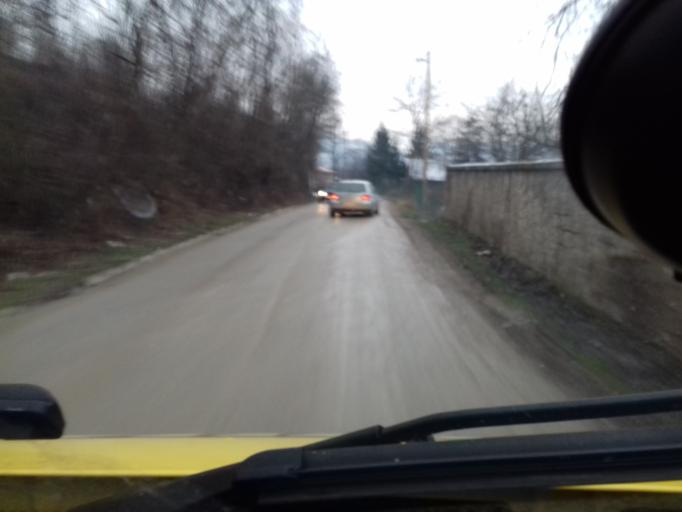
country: BA
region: Federation of Bosnia and Herzegovina
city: Zenica
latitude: 44.1774
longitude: 17.9753
